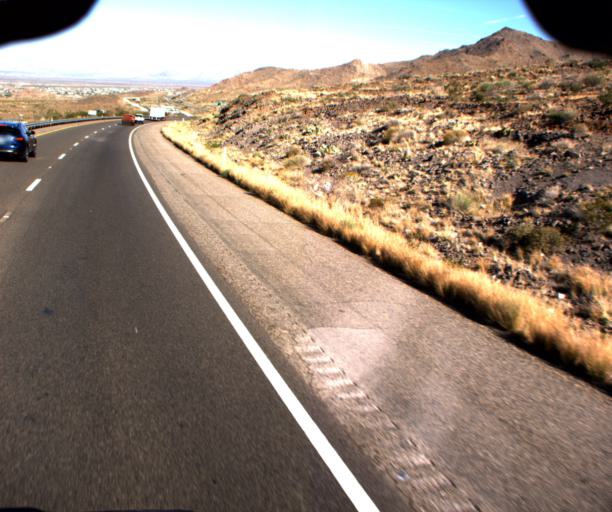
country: US
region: Arizona
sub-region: Mohave County
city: Kingman
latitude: 35.2122
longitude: -114.1114
